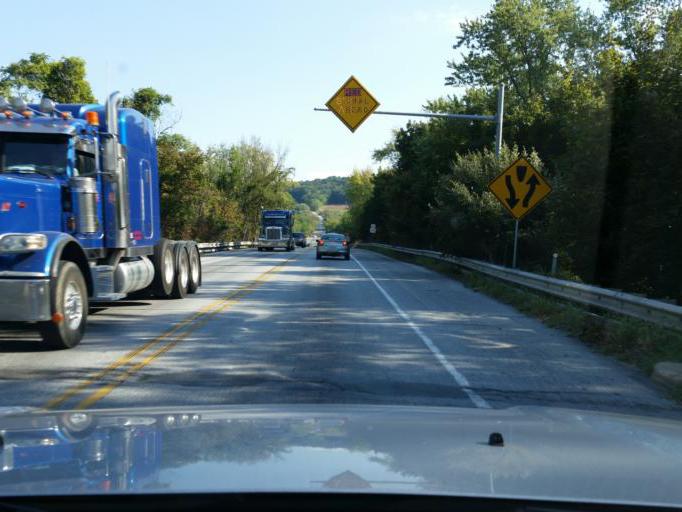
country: US
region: Pennsylvania
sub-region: Chester County
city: Atglen
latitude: 39.9503
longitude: -75.9708
